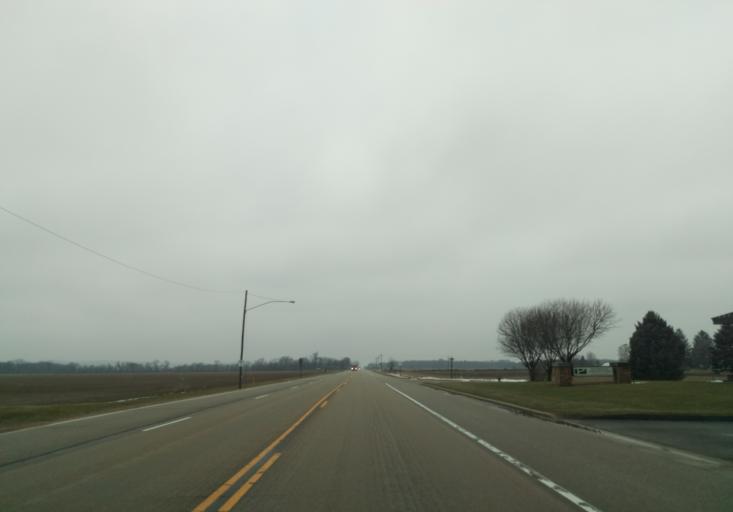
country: US
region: Wisconsin
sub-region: Dane County
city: Mazomanie
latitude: 43.1616
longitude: -89.9130
